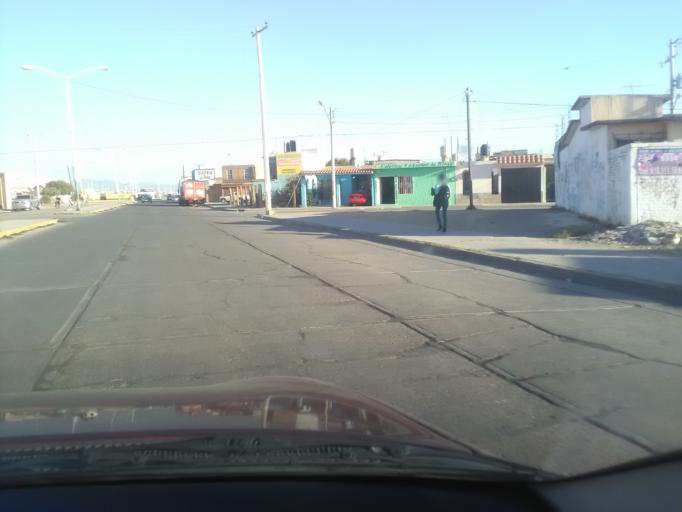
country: MX
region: Durango
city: Victoria de Durango
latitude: 24.0573
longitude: -104.5905
